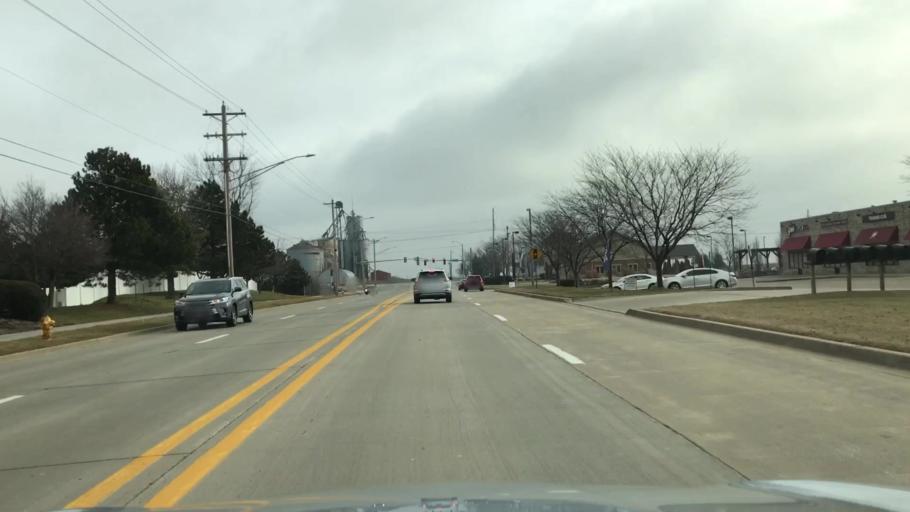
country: US
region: Illinois
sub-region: McLean County
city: Normal
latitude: 40.5027
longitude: -88.9059
